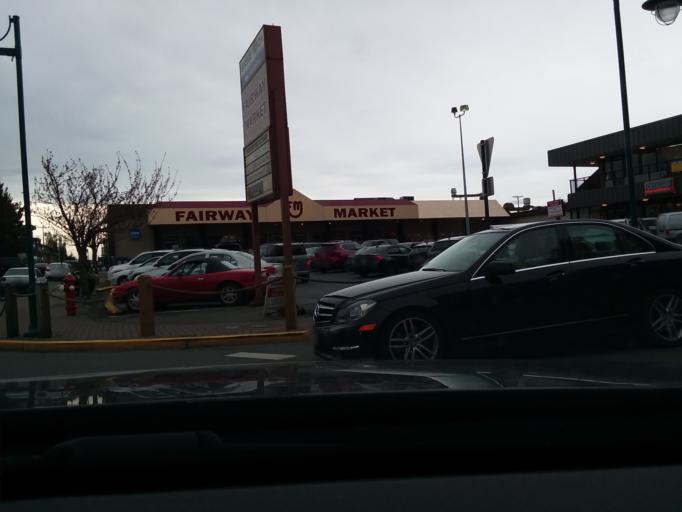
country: CA
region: British Columbia
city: North Saanich
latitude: 48.6489
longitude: -123.3955
